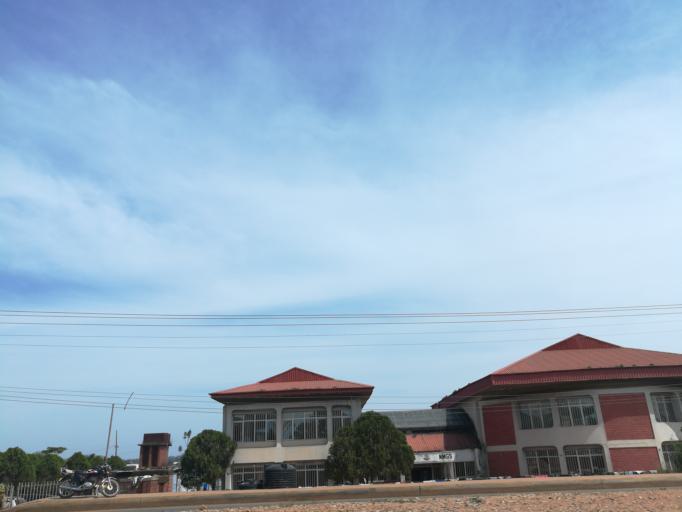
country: NG
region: Plateau
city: Bukuru
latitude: 9.7674
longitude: 8.8600
